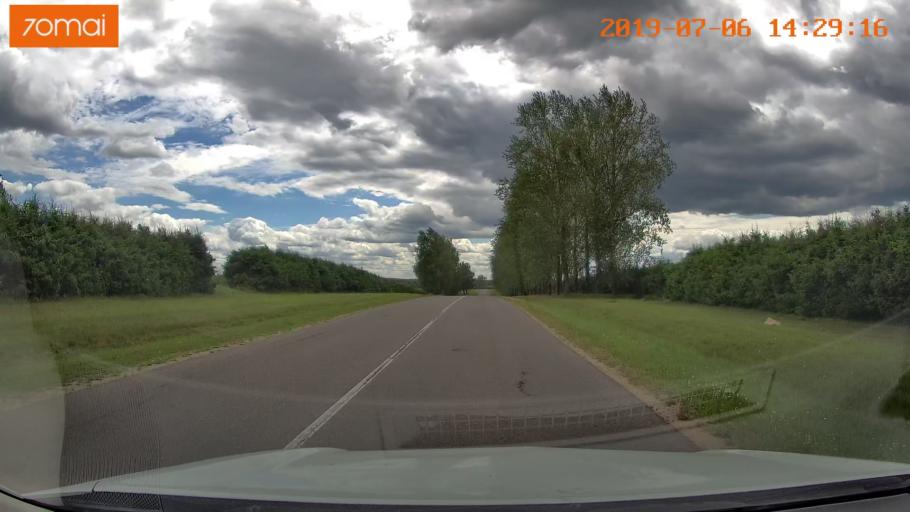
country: BY
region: Minsk
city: Ivyanyets
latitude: 53.9364
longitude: 26.7977
